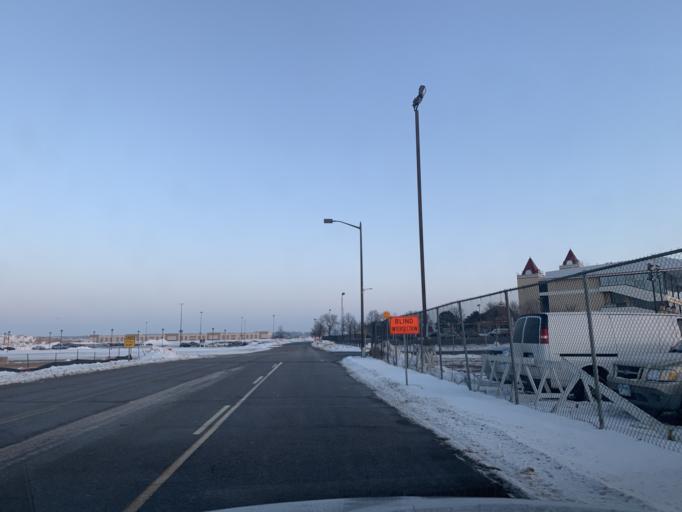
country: US
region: Minnesota
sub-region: Scott County
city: Shakopee
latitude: 44.7885
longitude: -93.4847
